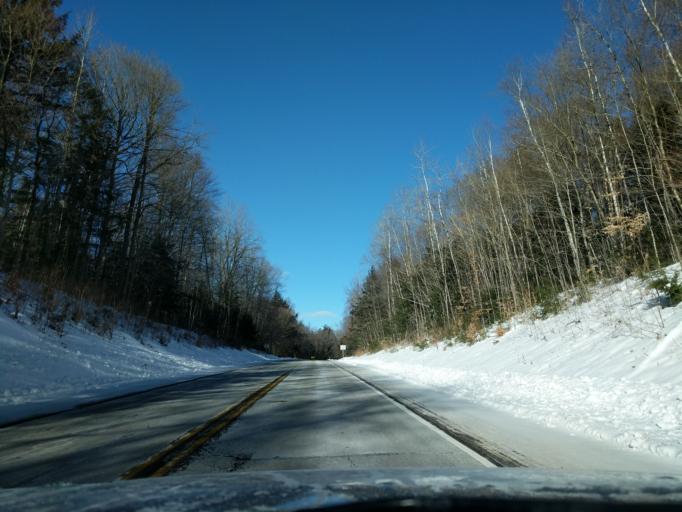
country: US
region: Wisconsin
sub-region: Menominee County
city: Keshena
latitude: 45.0980
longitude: -88.6340
